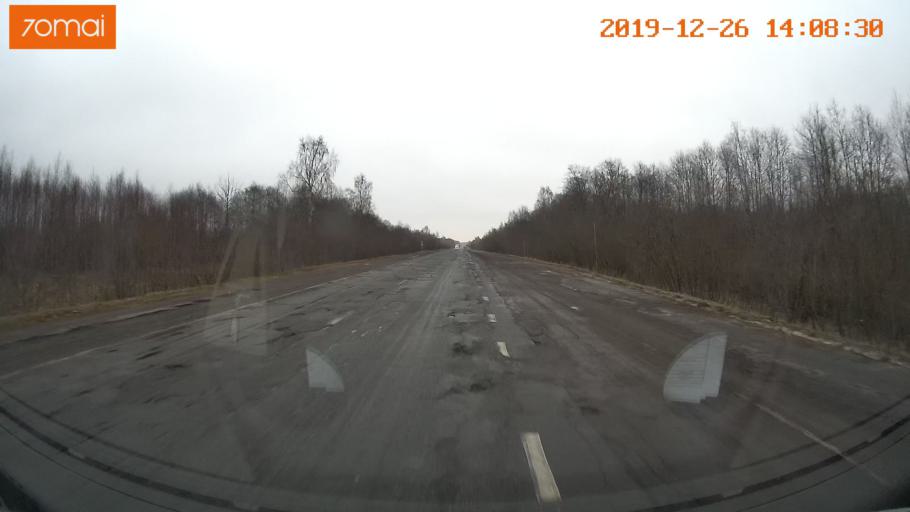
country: RU
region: Jaroslavl
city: Poshekhon'ye
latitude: 58.5087
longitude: 38.9137
